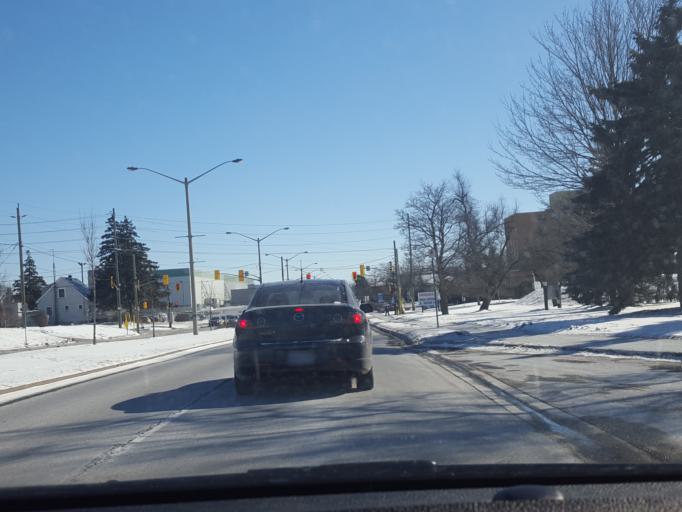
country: CA
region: Ontario
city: Cambridge
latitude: 43.3786
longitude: -80.3276
